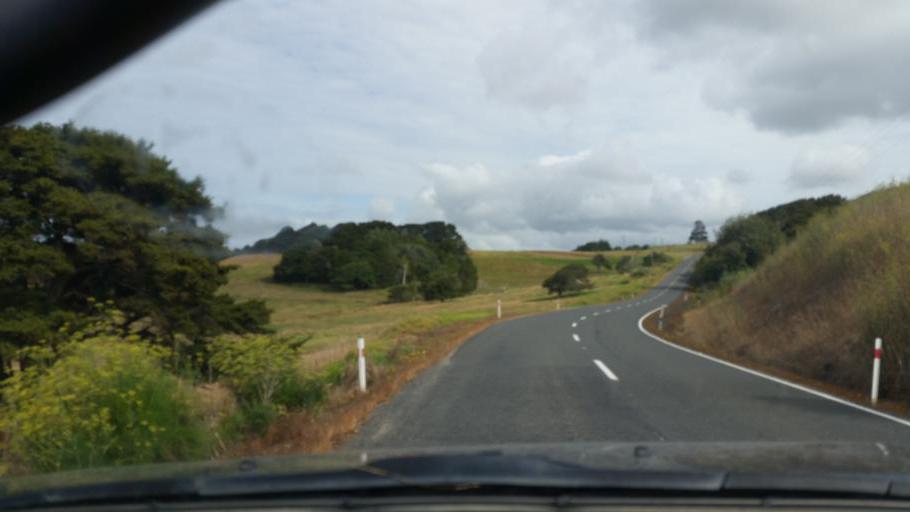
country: NZ
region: Northland
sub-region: Kaipara District
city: Dargaville
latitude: -35.9617
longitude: 173.9267
